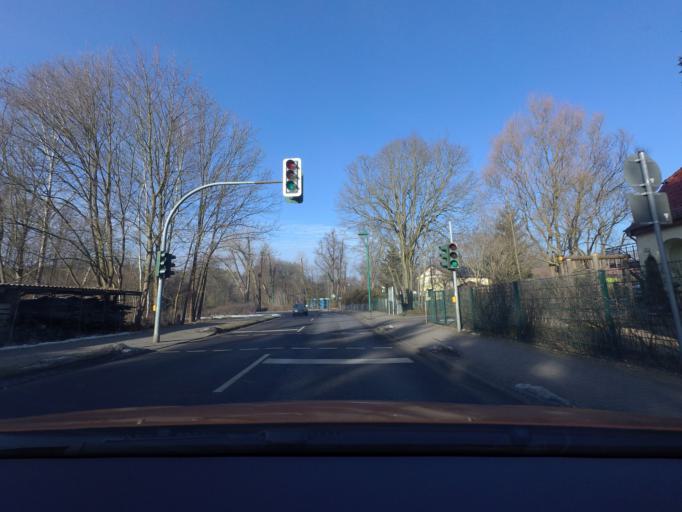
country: DE
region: Brandenburg
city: Glienicke
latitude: 52.6887
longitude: 13.3686
